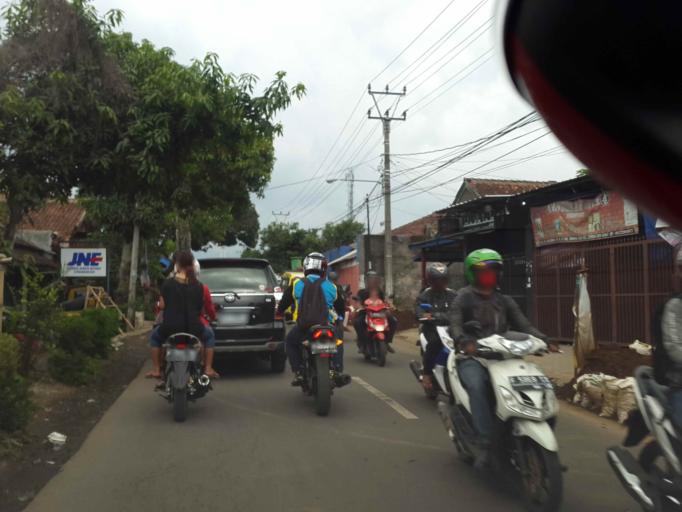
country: ID
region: West Java
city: Sukabumi
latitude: -6.9537
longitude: 106.9114
